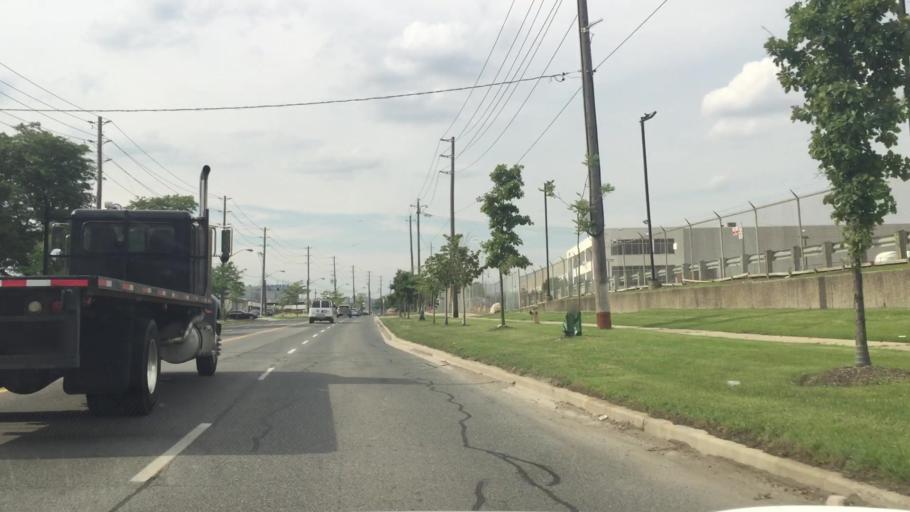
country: CA
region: Ontario
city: Concord
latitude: 43.7588
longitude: -79.5390
